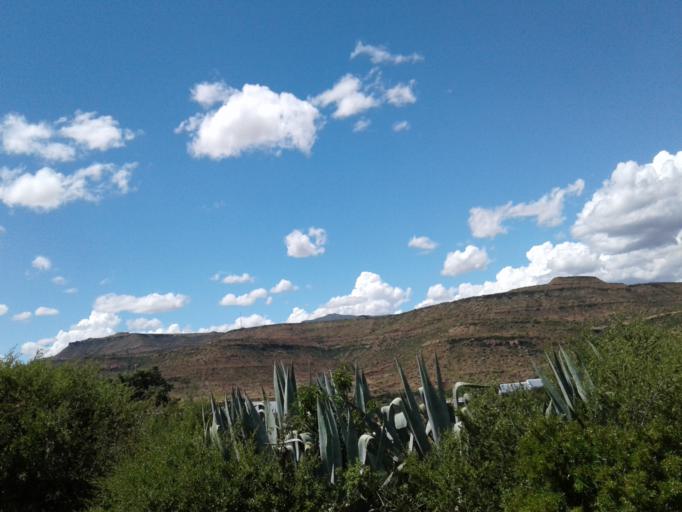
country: LS
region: Quthing
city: Quthing
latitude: -30.3705
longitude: 27.5500
